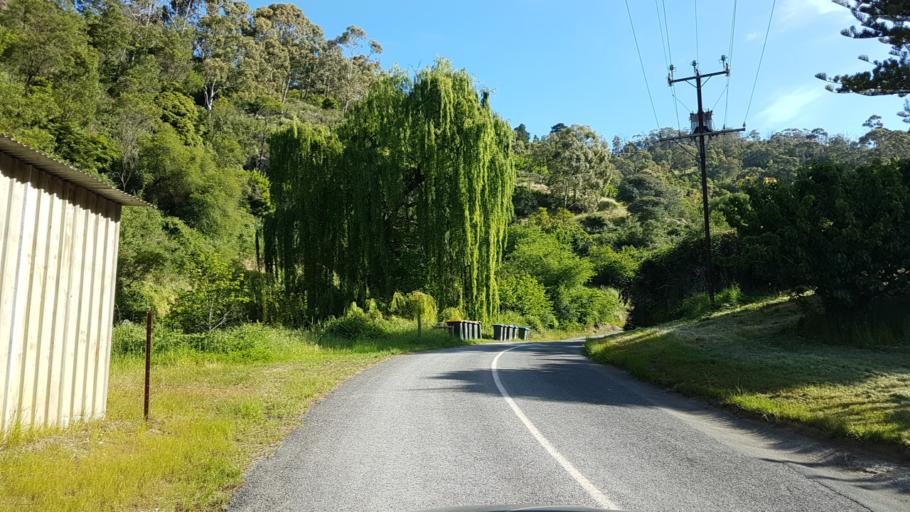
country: AU
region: South Australia
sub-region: Adelaide Hills
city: Adelaide Hills
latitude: -34.9081
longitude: 138.7745
